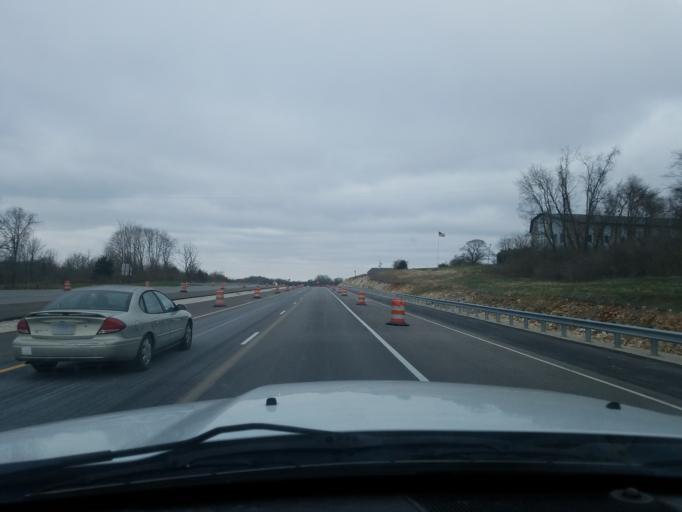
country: US
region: Indiana
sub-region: Monroe County
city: Bloomington
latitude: 39.2043
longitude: -86.5537
